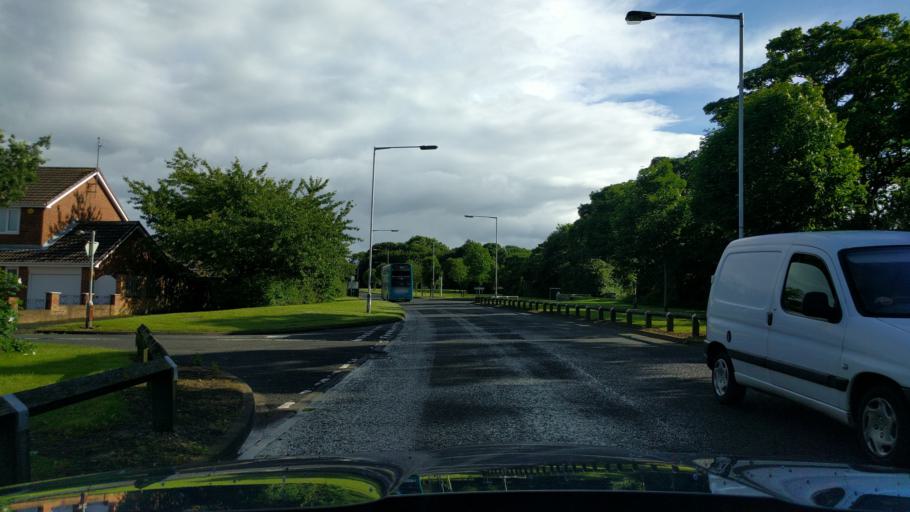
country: GB
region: England
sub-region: Northumberland
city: Cramlington
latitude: 55.0972
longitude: -1.5900
